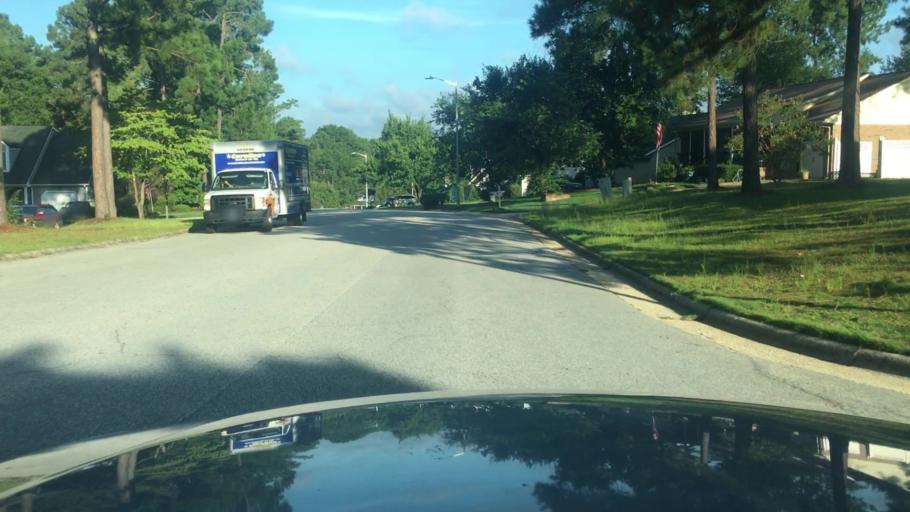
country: US
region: North Carolina
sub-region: Cumberland County
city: Eastover
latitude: 35.1406
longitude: -78.8769
